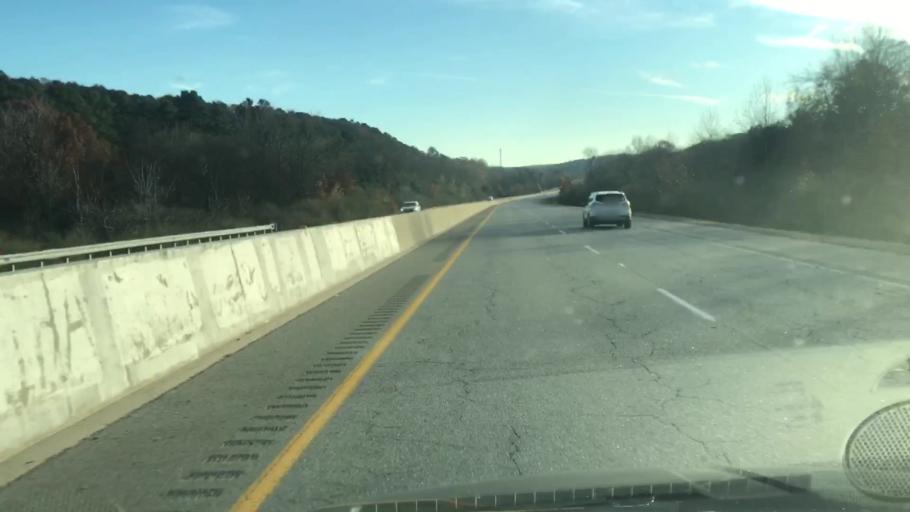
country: US
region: Arkansas
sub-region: Garland County
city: Hot Springs
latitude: 34.4846
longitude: -92.9816
